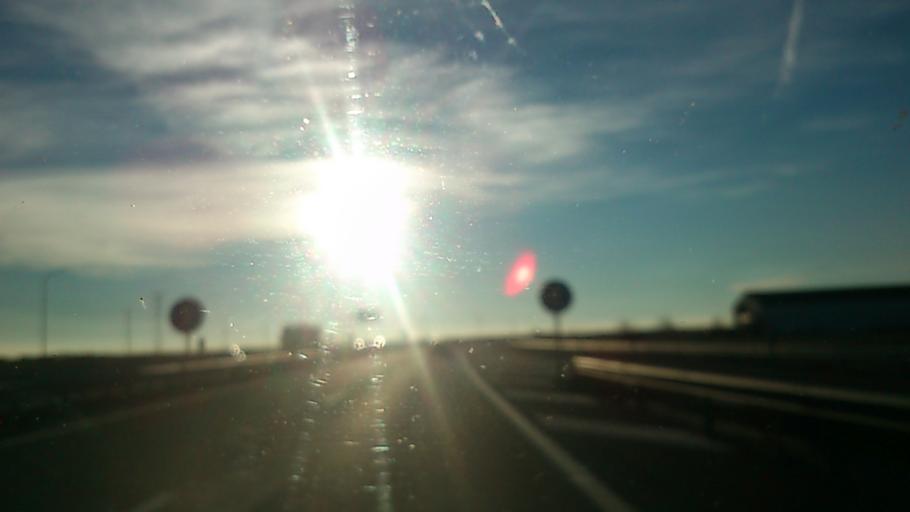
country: ES
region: Castille-La Mancha
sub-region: Provincia de Guadalajara
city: Ledanca
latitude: 40.8586
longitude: -2.8378
